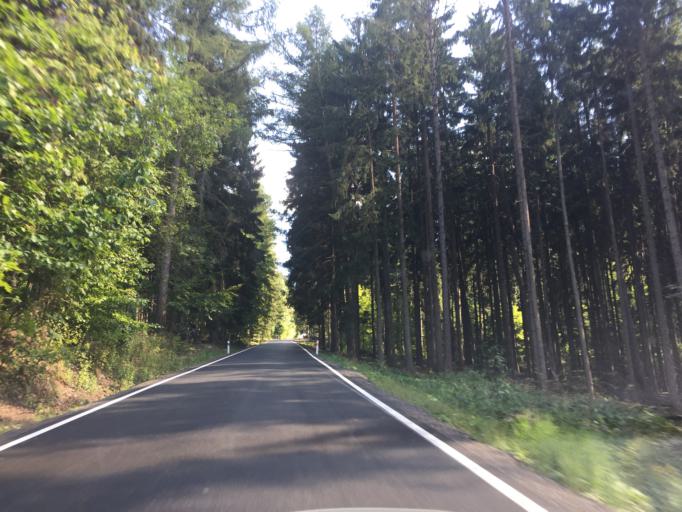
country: CZ
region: Liberecky
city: Mala Skala
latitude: 50.6364
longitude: 15.2097
